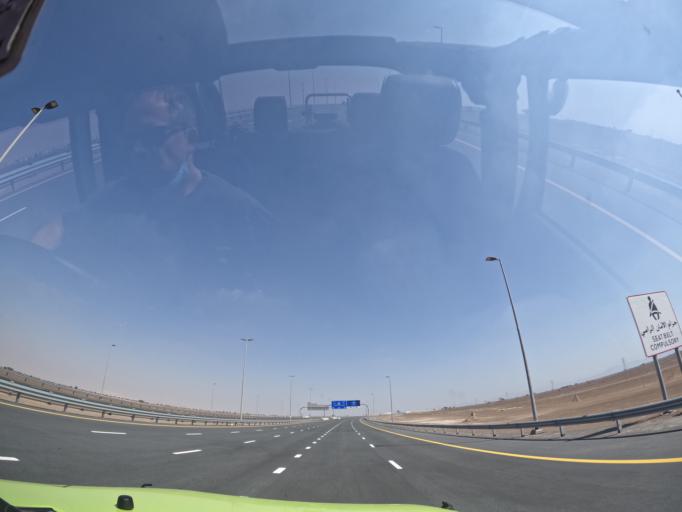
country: AE
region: Ash Shariqah
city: Adh Dhayd
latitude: 24.9211
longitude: 55.8056
